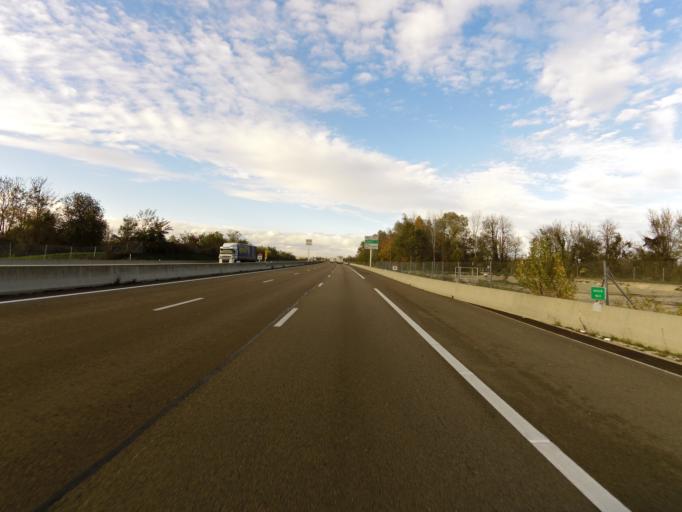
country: FR
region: Bourgogne
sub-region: Departement de la Cote-d'Or
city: Couternon
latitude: 47.3326
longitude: 5.1684
